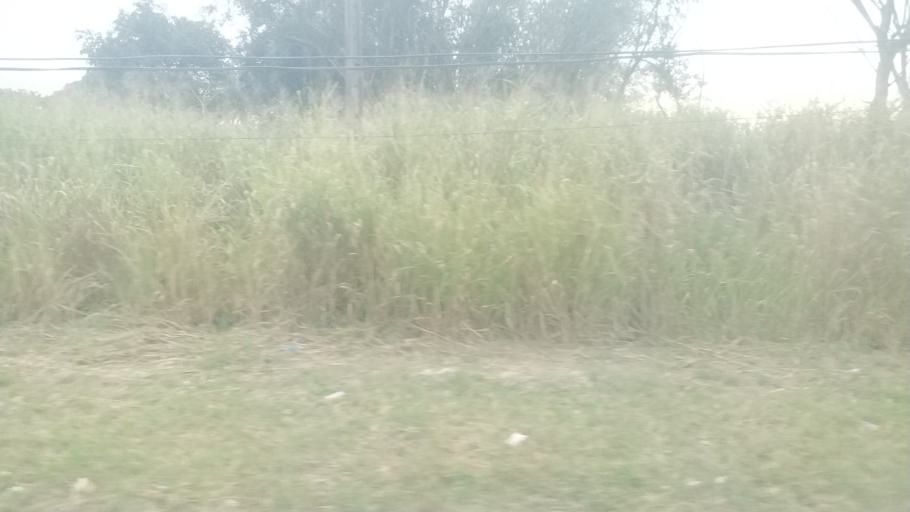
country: BR
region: Rio de Janeiro
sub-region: Seropedica
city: Seropedica
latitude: -22.7692
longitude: -43.6750
